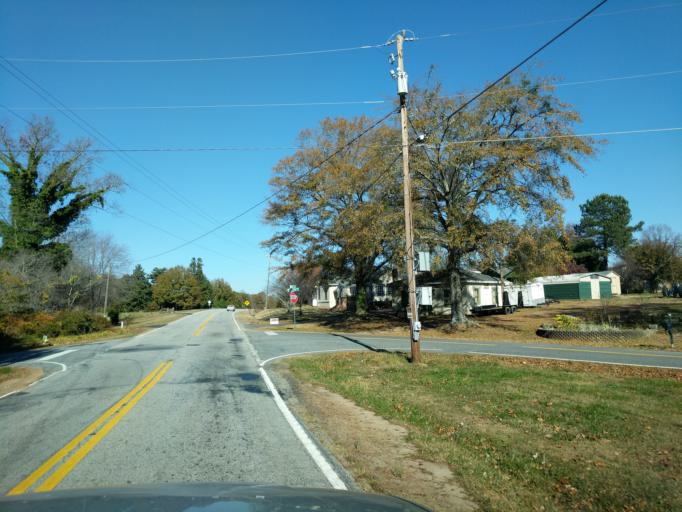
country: US
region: South Carolina
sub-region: Spartanburg County
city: Inman Mills
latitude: 35.0353
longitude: -82.1852
